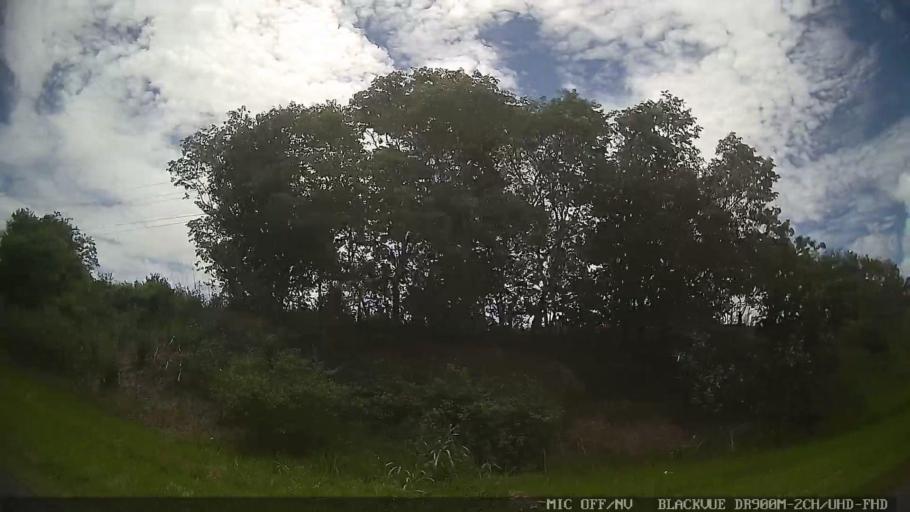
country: BR
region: Sao Paulo
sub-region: Conchas
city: Conchas
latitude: -23.0553
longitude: -47.9607
